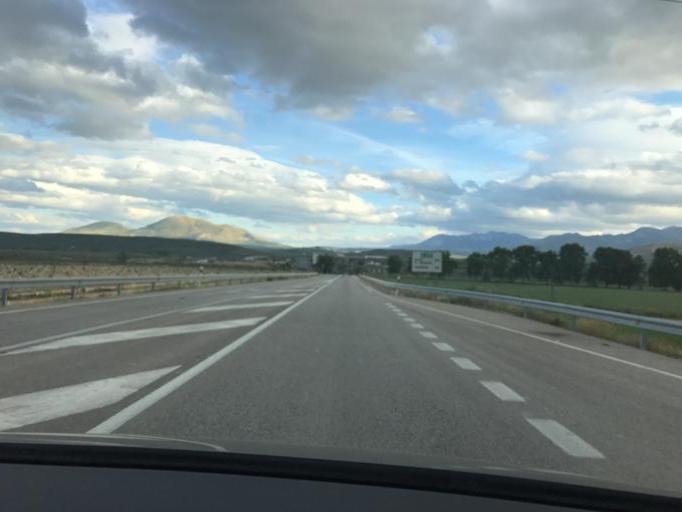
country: ES
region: Andalusia
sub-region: Provincia de Jaen
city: Jodar
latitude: 37.9257
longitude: -3.3536
